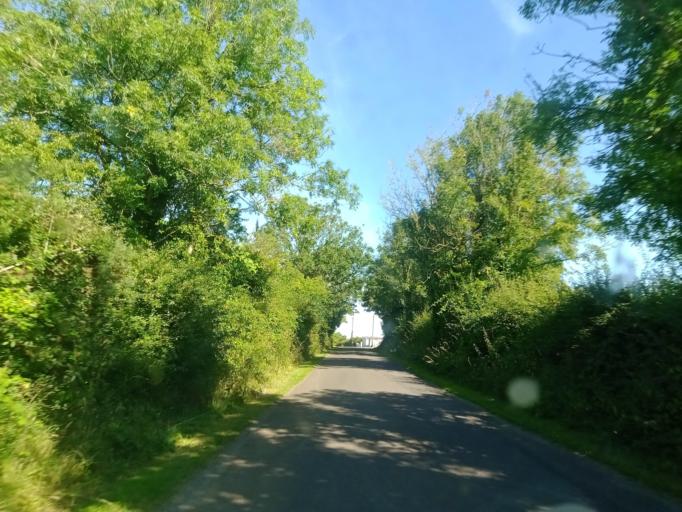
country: IE
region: Leinster
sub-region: Kilkenny
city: Ballyragget
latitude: 52.7812
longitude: -7.4175
